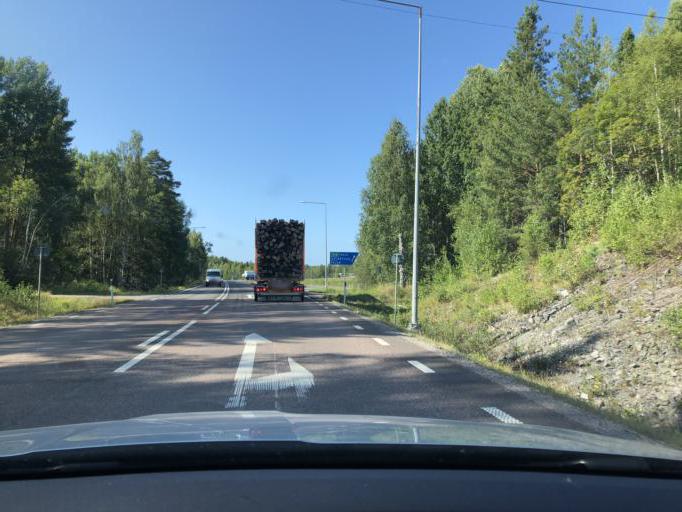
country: SE
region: Dalarna
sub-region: Faluns Kommun
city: Falun
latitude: 60.5843
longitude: 15.7719
